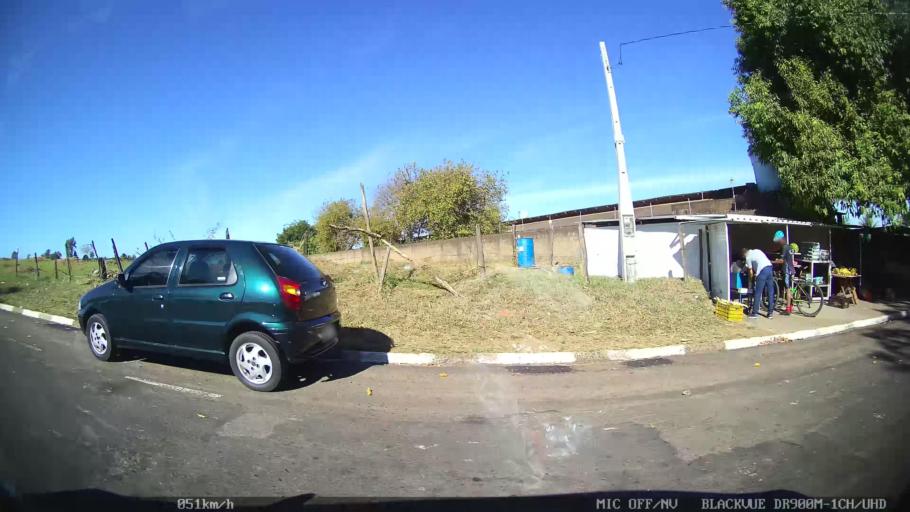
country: BR
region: Sao Paulo
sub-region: Franca
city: Franca
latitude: -20.5571
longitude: -47.3834
